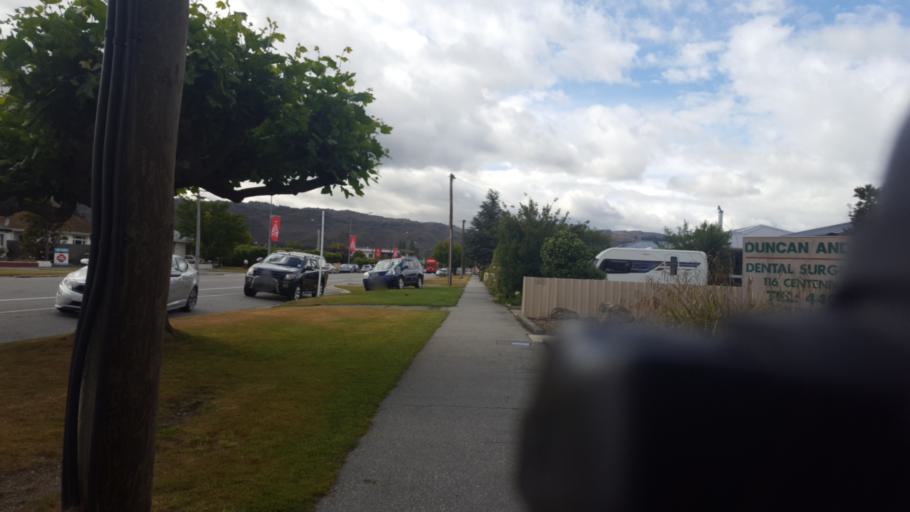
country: NZ
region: Otago
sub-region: Queenstown-Lakes District
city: Wanaka
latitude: -45.2484
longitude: 169.3846
